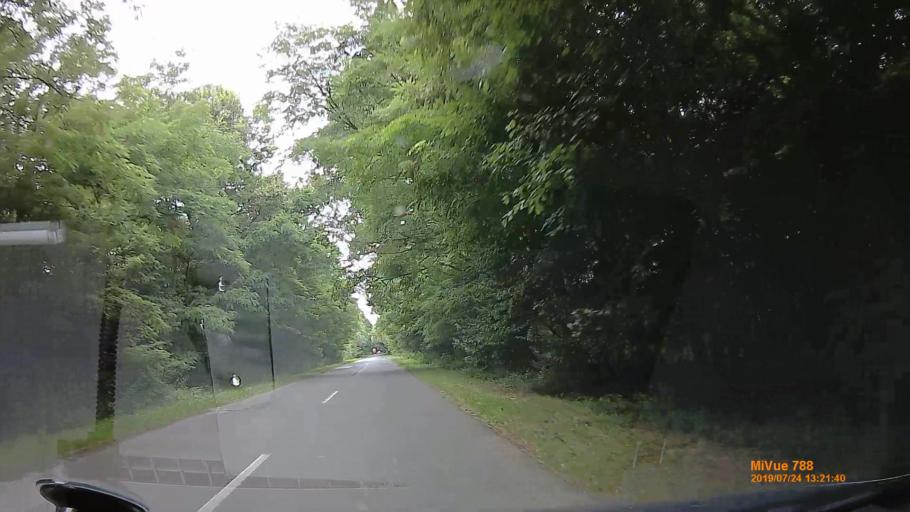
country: HU
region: Szabolcs-Szatmar-Bereg
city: Vasarosnameny
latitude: 48.2115
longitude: 22.4133
